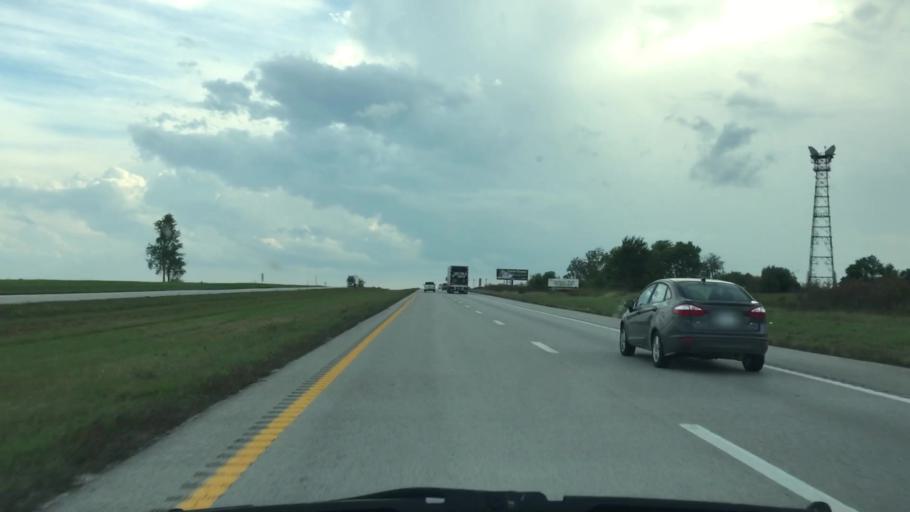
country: US
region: Missouri
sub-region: Clinton County
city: Cameron
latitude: 39.8373
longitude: -94.1841
